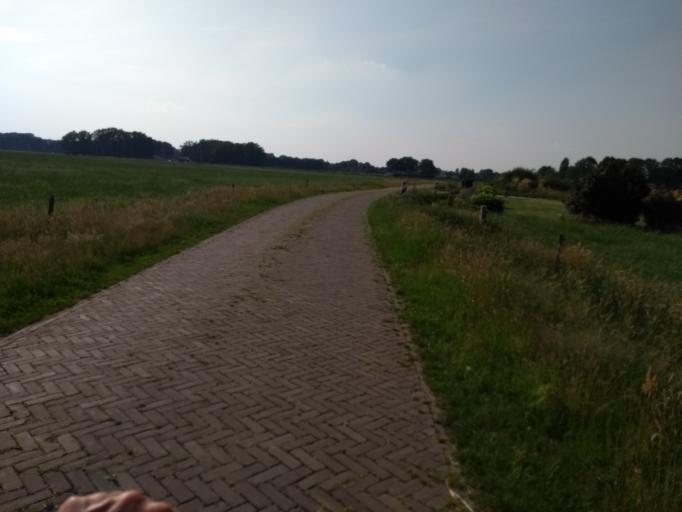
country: NL
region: Overijssel
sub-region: Gemeente Tubbergen
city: Tubbergen
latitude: 52.3676
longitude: 6.7497
